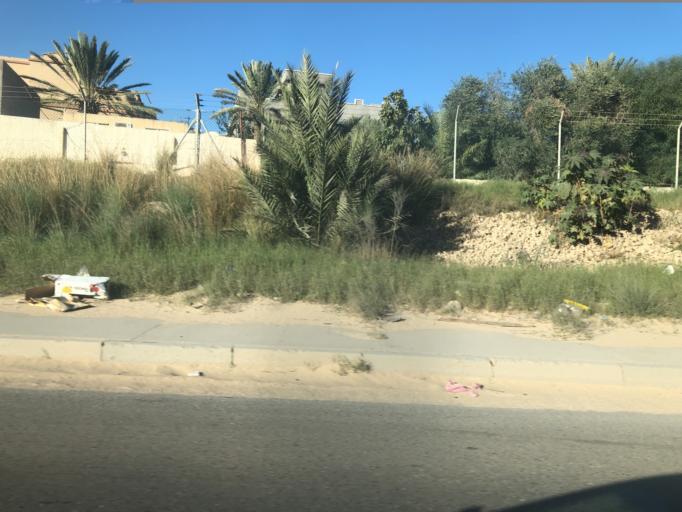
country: LY
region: Tripoli
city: Tagiura
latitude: 32.8690
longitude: 13.2762
